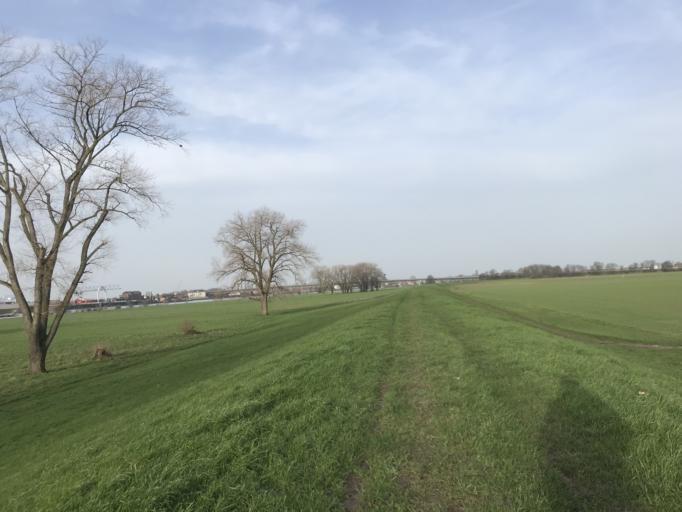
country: DE
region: North Rhine-Westphalia
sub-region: Regierungsbezirk Dusseldorf
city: Meerbusch
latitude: 51.3486
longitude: 6.6785
